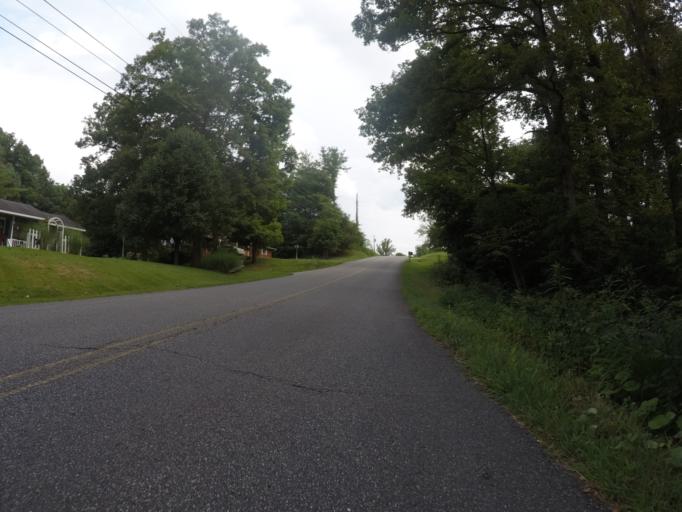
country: US
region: Kentucky
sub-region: Boyd County
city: Meads
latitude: 38.4200
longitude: -82.7076
